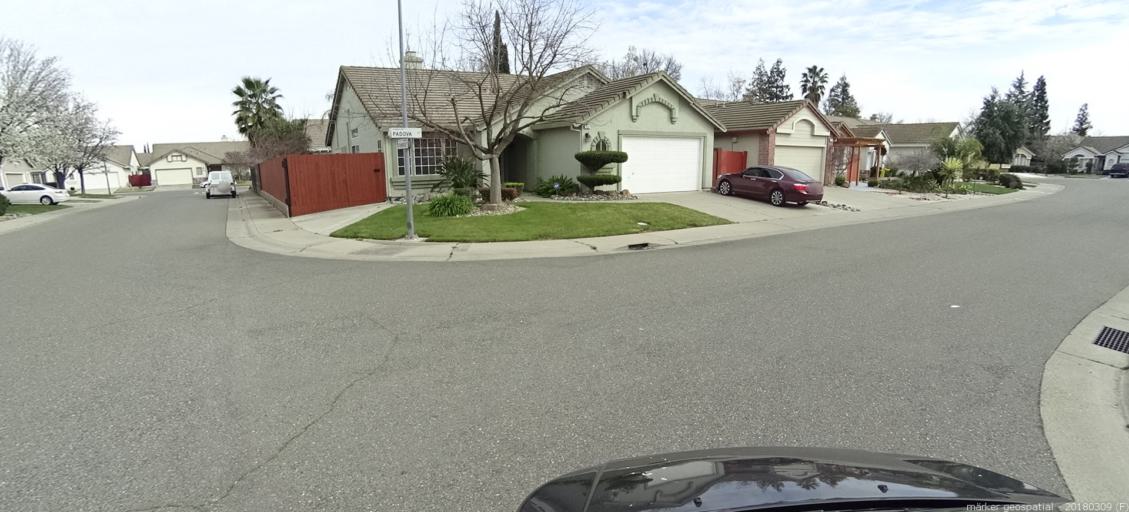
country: US
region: California
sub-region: Sacramento County
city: Vineyard
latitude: 38.4619
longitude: -121.3703
